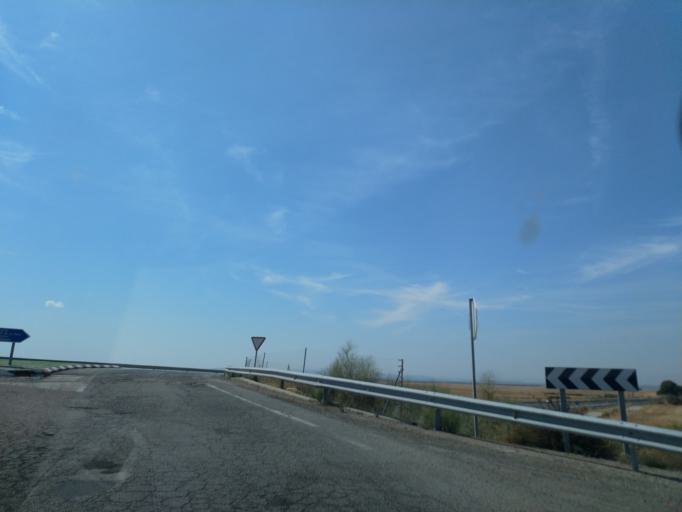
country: ES
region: Extremadura
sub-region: Provincia de Caceres
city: Berrocalejo
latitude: 39.8957
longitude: -5.3456
